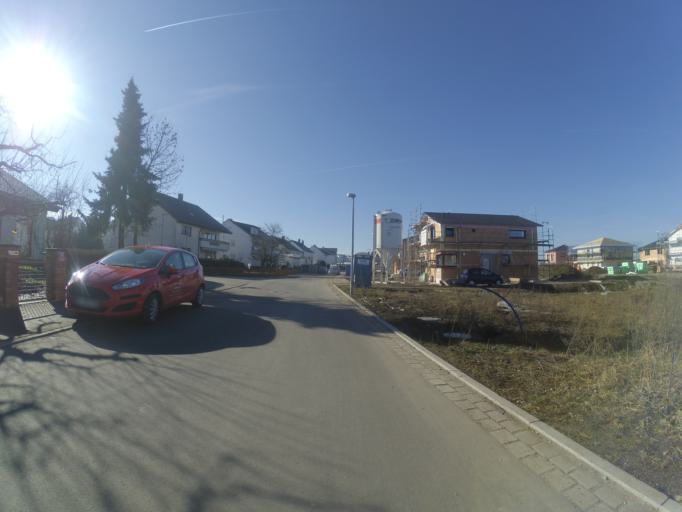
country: DE
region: Baden-Wuerttemberg
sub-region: Tuebingen Region
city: Erbach
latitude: 48.3079
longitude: 9.9047
